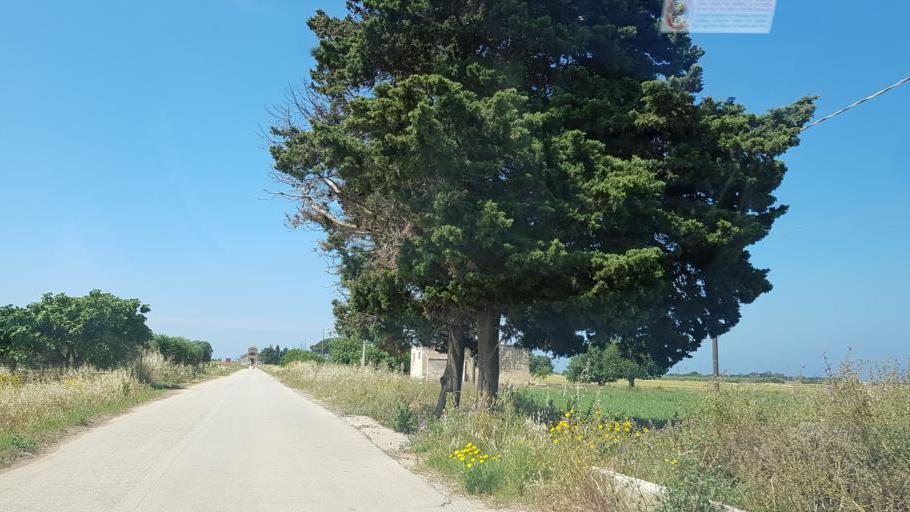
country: IT
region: Apulia
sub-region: Provincia di Brindisi
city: Brindisi
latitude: 40.6575
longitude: 17.8520
